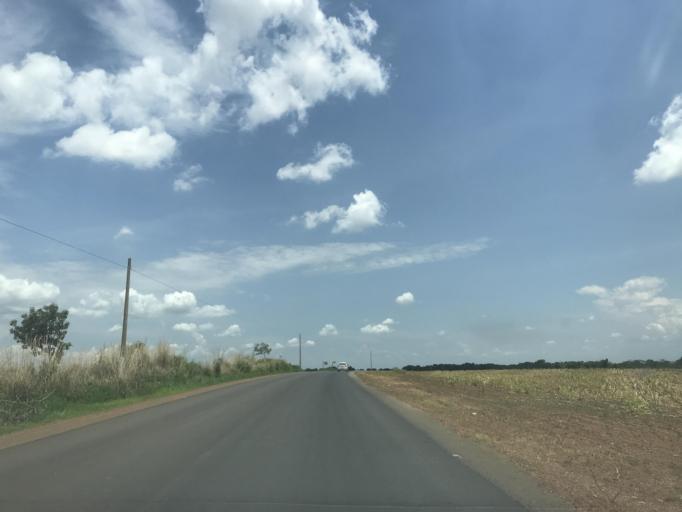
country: BR
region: Goias
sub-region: Bela Vista De Goias
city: Bela Vista de Goias
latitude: -17.0847
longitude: -48.6541
